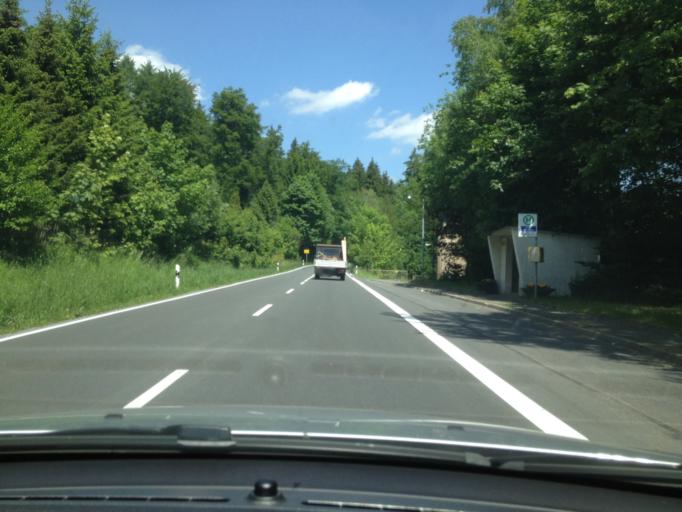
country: DE
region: Saxony
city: Ehrenfriedersdorf
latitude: 50.6635
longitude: 12.9646
